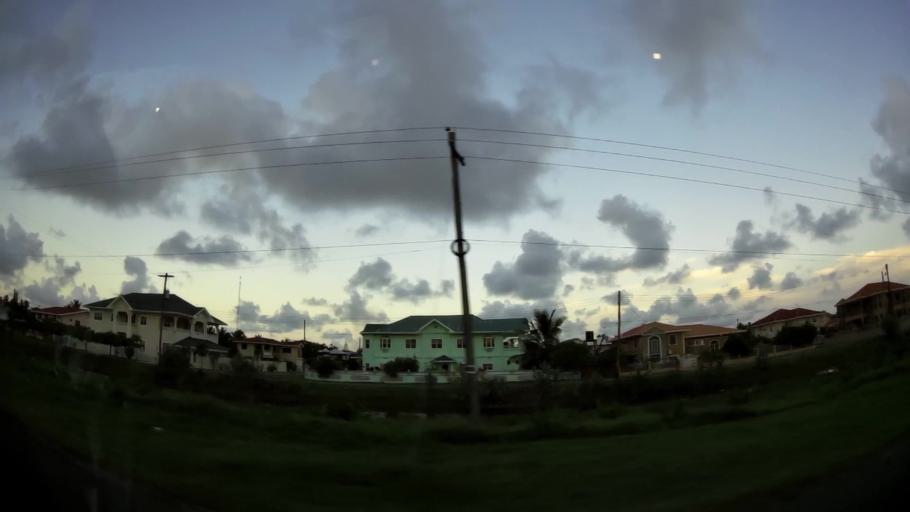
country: GY
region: Demerara-Mahaica
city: Georgetown
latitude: 6.8149
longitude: -58.0992
